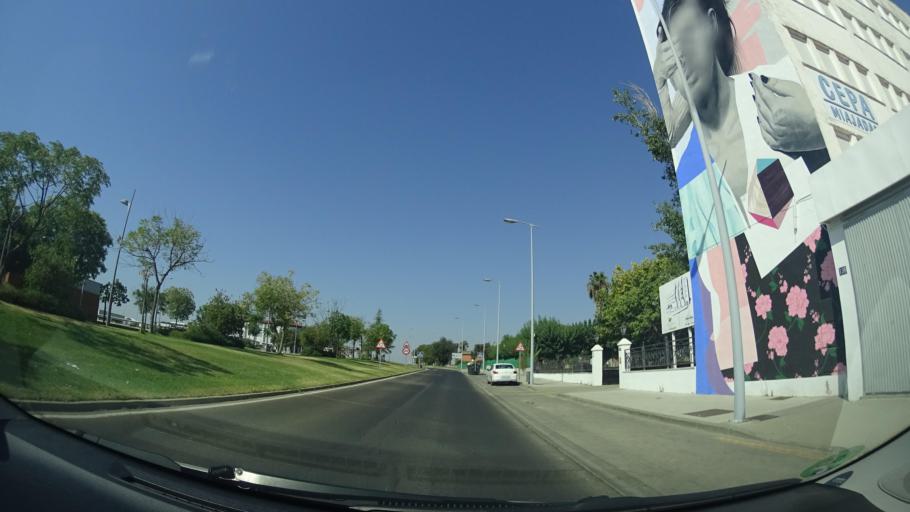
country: ES
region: Extremadura
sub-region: Provincia de Caceres
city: Miajadas
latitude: 39.1444
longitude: -5.9239
